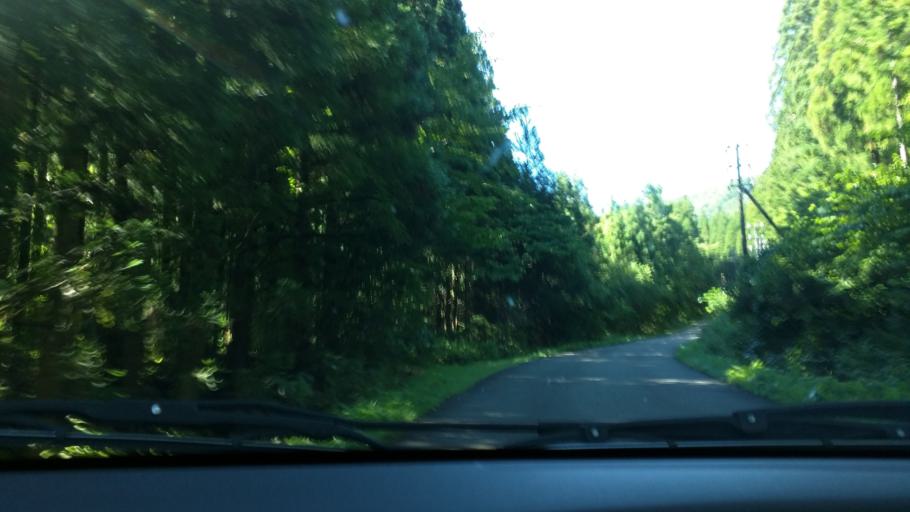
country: JP
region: Fukushima
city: Inawashiro
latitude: 37.3581
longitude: 140.0570
